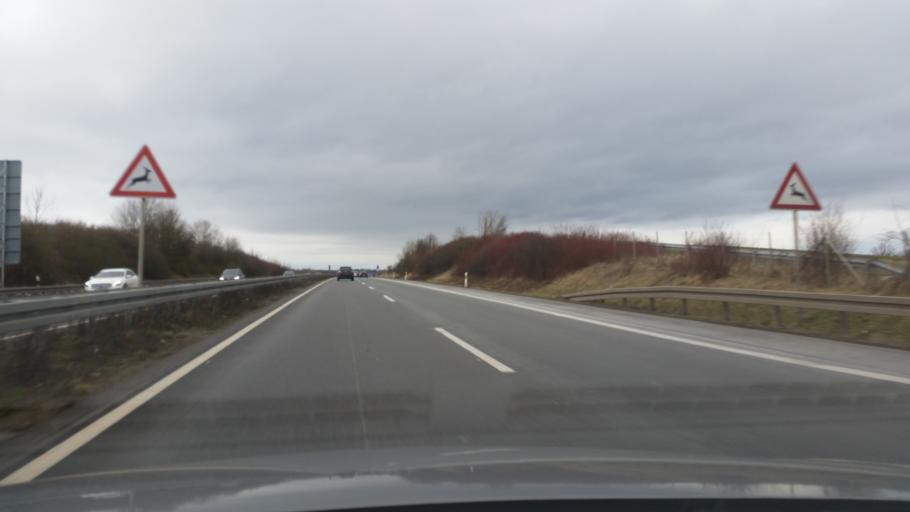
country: DE
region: Lower Saxony
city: Schladen
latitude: 52.0297
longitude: 10.5197
